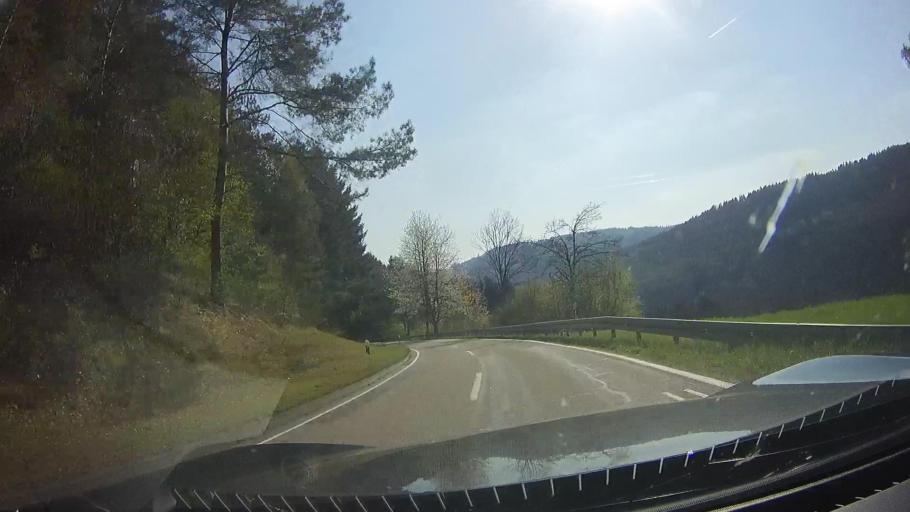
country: DE
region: Hesse
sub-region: Regierungsbezirk Darmstadt
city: Rothenberg
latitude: 49.4757
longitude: 8.9049
